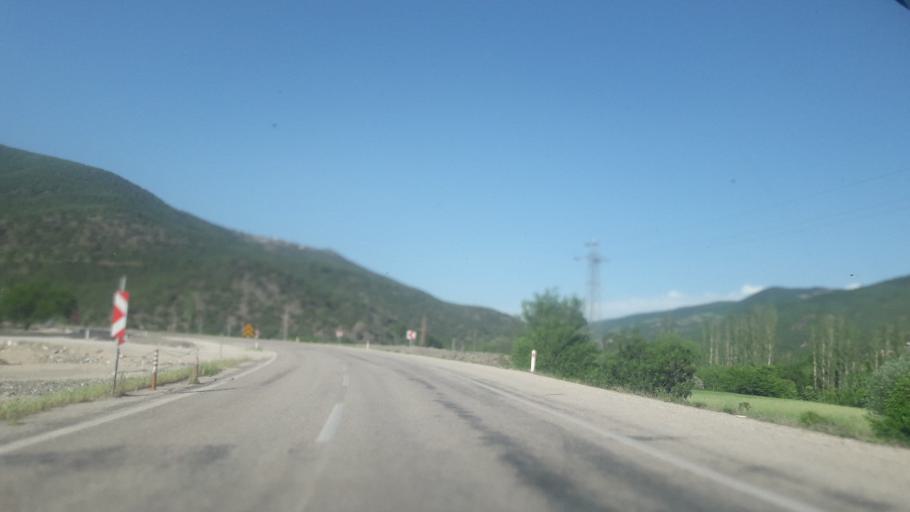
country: TR
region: Tokat
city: Turhal
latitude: 40.4780
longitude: 36.1539
